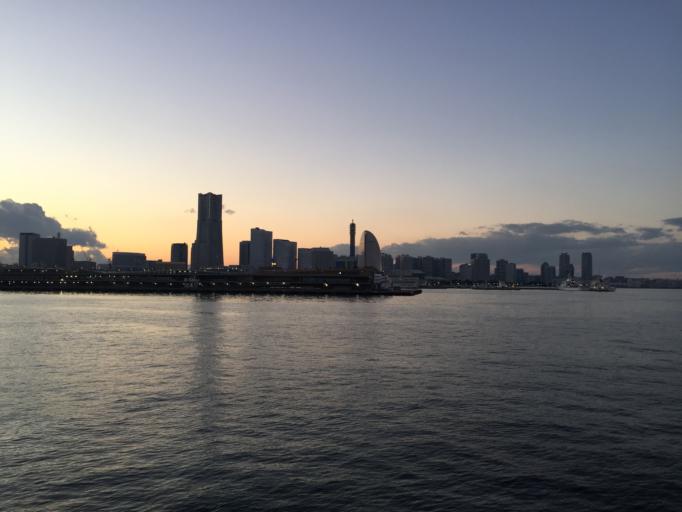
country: JP
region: Kanagawa
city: Yokohama
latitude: 35.4517
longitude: 139.6532
